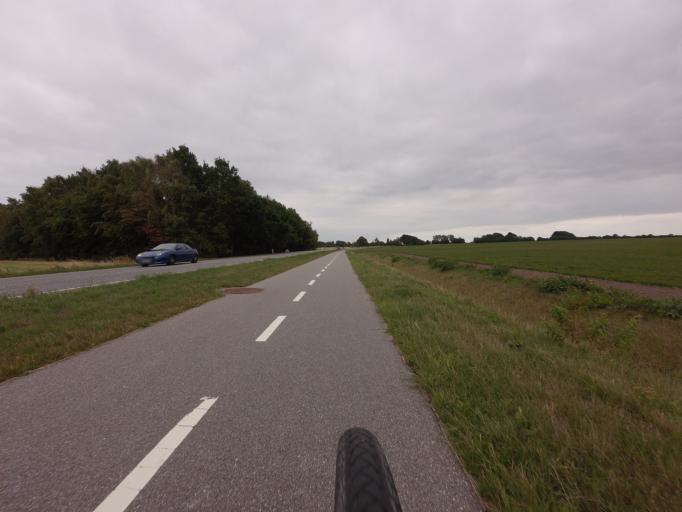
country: DK
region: Zealand
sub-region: Stevns Kommune
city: Store Heddinge
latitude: 55.2941
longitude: 12.3913
